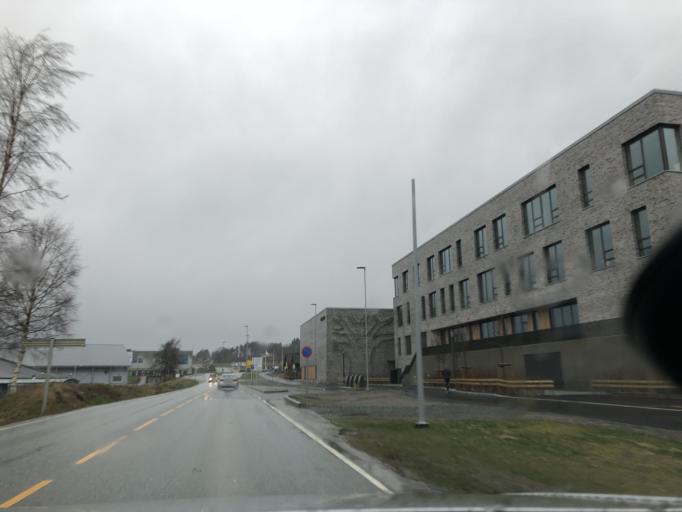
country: NO
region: Rogaland
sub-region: Strand
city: Tau
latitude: 59.0626
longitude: 5.9226
